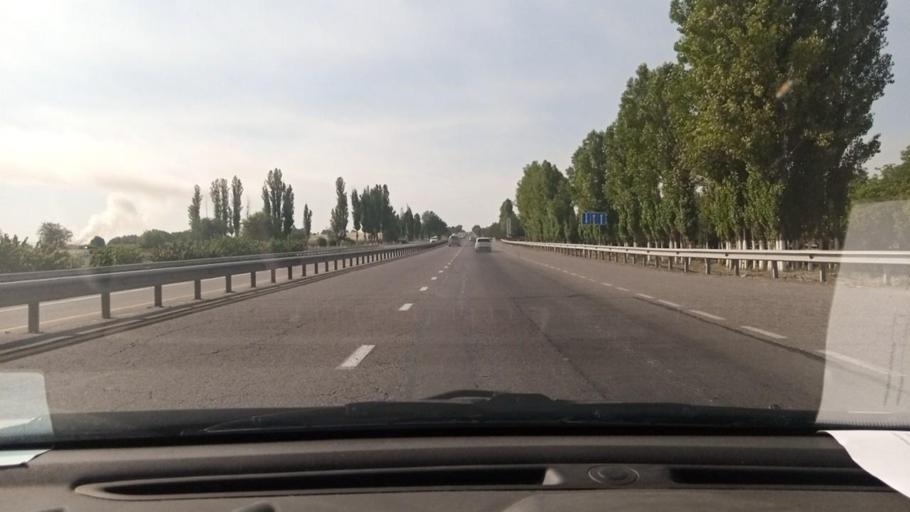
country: UZ
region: Toshkent
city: Tuytepa
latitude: 41.1192
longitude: 69.4427
